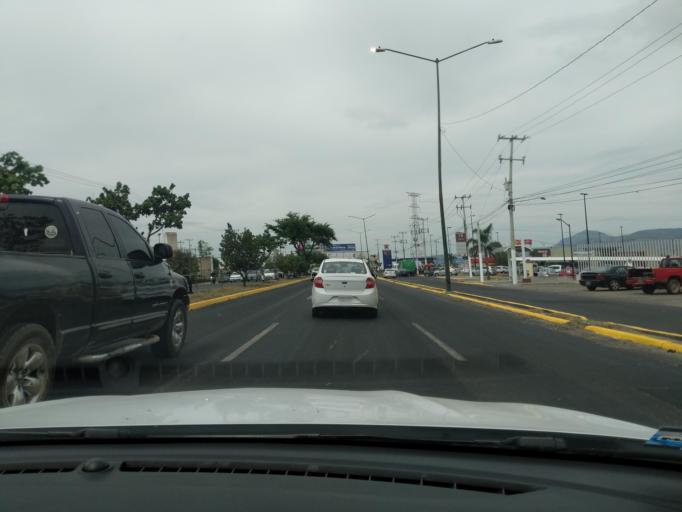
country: MX
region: Jalisco
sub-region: Zapopan
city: La Cuchilla (Extramuros de Tesistan)
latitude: 20.7755
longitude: -103.4546
